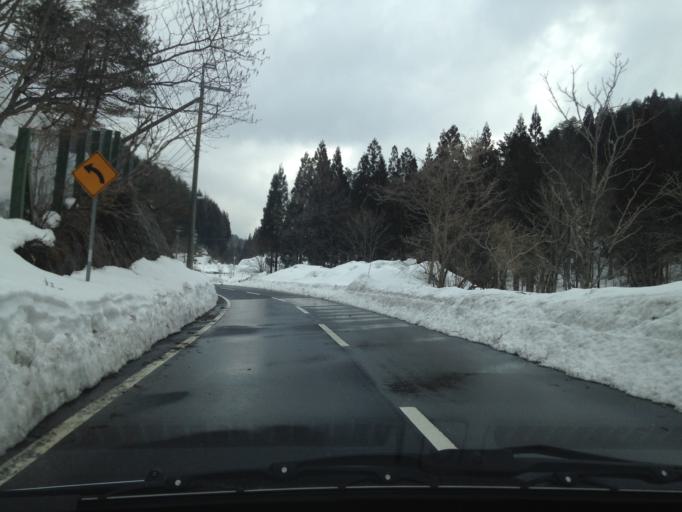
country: JP
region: Hyogo
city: Yamazakicho-nakabirose
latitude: 35.2114
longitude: 134.3944
